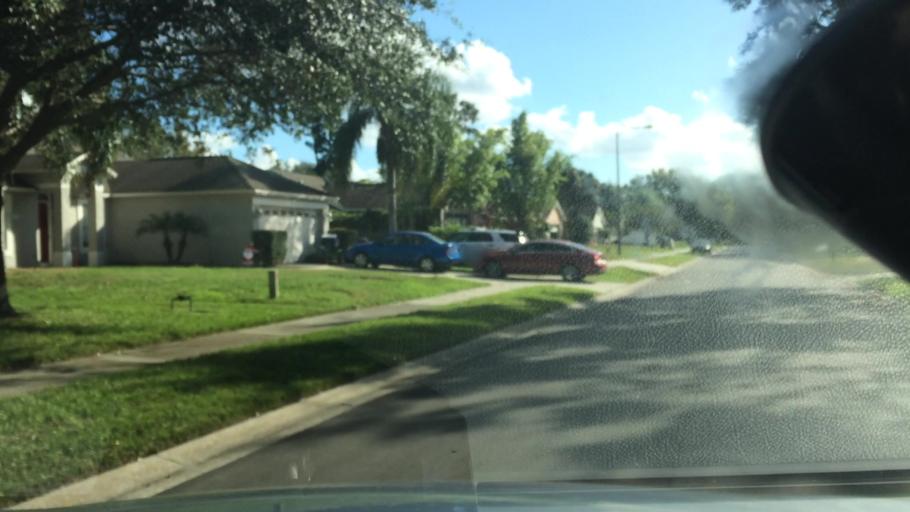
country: US
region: Florida
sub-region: Osceola County
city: Saint Cloud
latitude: 28.2117
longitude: -81.2843
